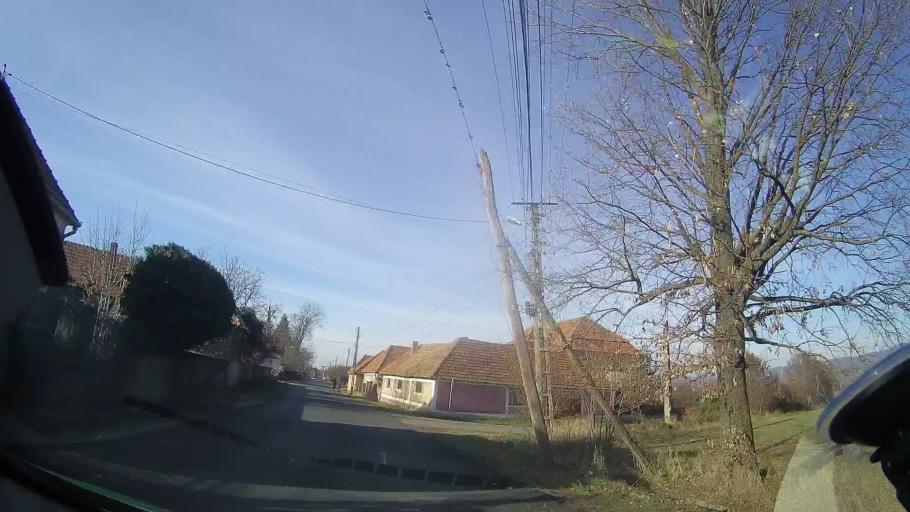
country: RO
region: Bihor
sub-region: Comuna Magesti
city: Magesti
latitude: 47.0128
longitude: 22.4436
